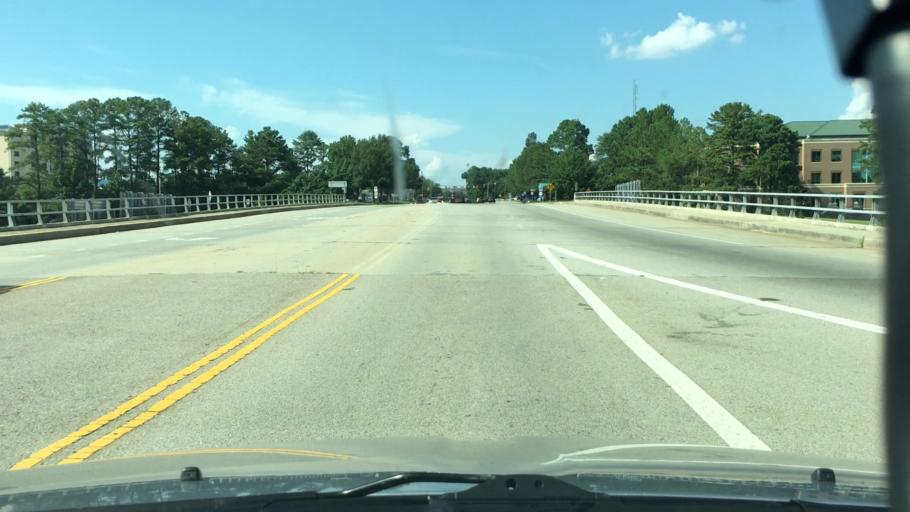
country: US
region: South Carolina
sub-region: Lexington County
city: West Columbia
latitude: 34.0120
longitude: -81.0761
